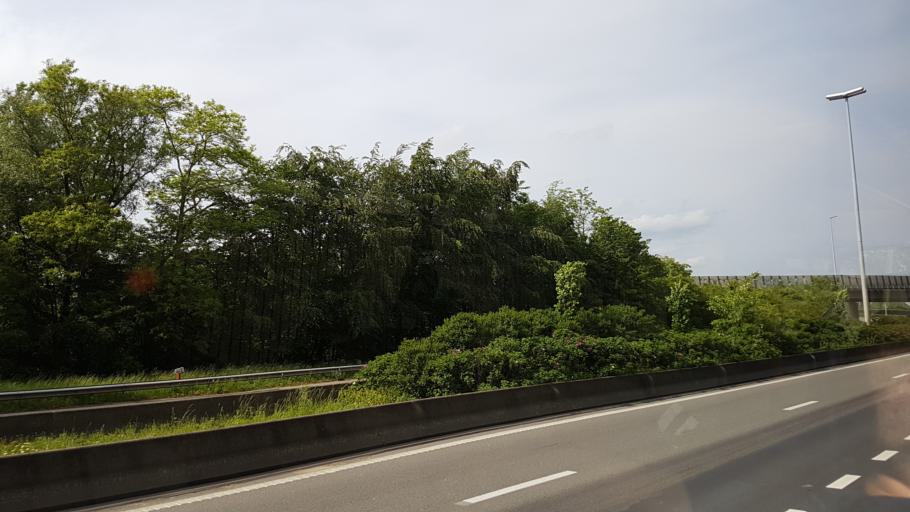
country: BE
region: Flanders
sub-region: Provincie Antwerpen
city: Kapellen
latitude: 51.2820
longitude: 4.4081
